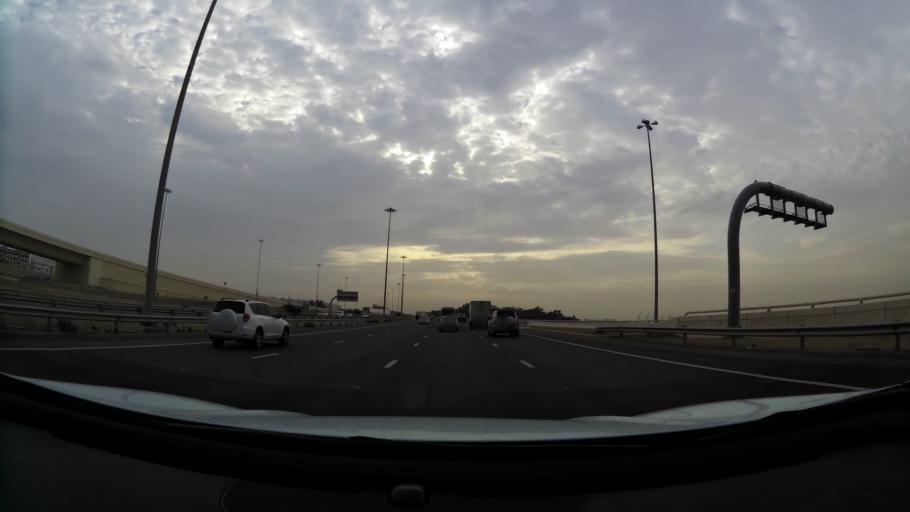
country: AE
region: Abu Dhabi
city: Abu Dhabi
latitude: 24.3070
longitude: 54.6042
